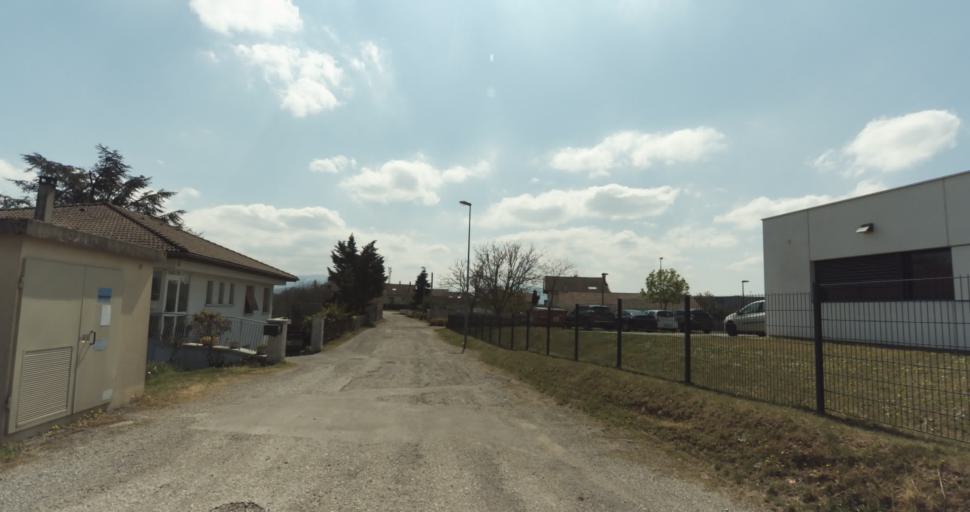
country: FR
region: Rhone-Alpes
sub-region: Departement de l'Isere
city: Saint-Marcellin
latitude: 45.1370
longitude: 5.3230
